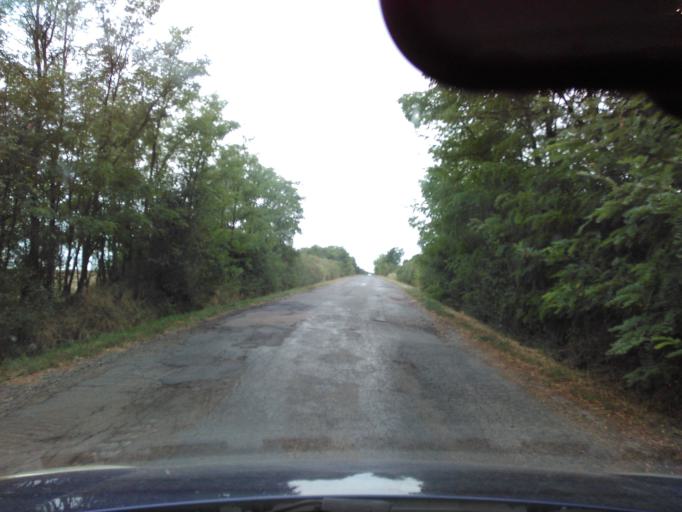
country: HU
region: Nograd
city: Szurdokpuspoki
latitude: 47.8910
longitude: 19.6672
